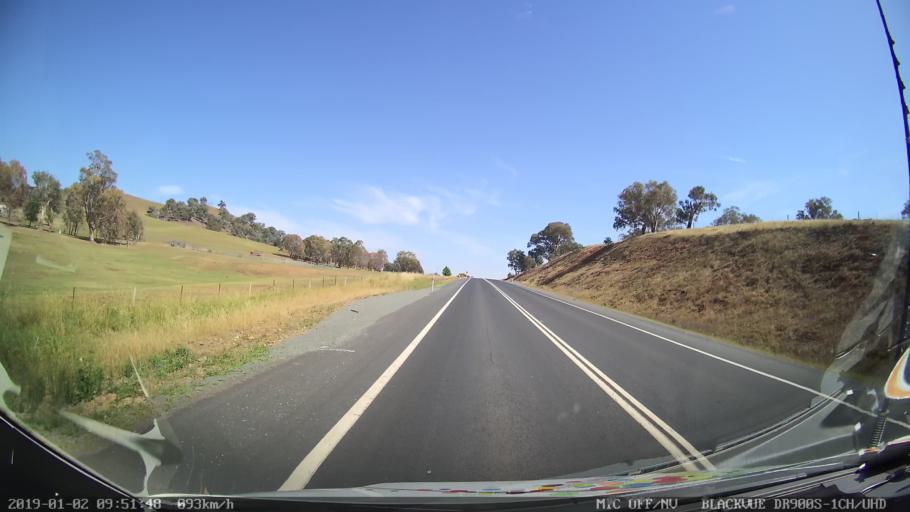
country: AU
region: New South Wales
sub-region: Tumut Shire
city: Tumut
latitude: -35.2687
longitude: 148.2114
